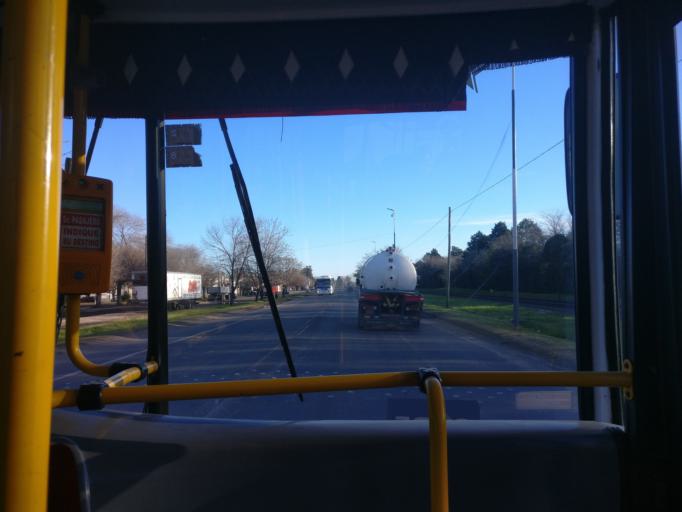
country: AR
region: Buenos Aires
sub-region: Partido de Ezeiza
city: Ezeiza
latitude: -34.9148
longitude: -58.6000
